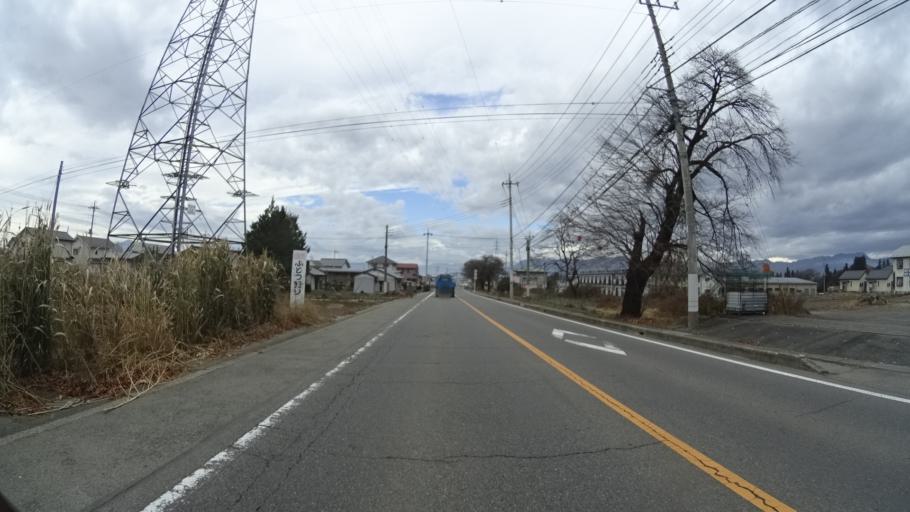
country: JP
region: Gunma
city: Numata
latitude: 36.6637
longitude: 139.1250
